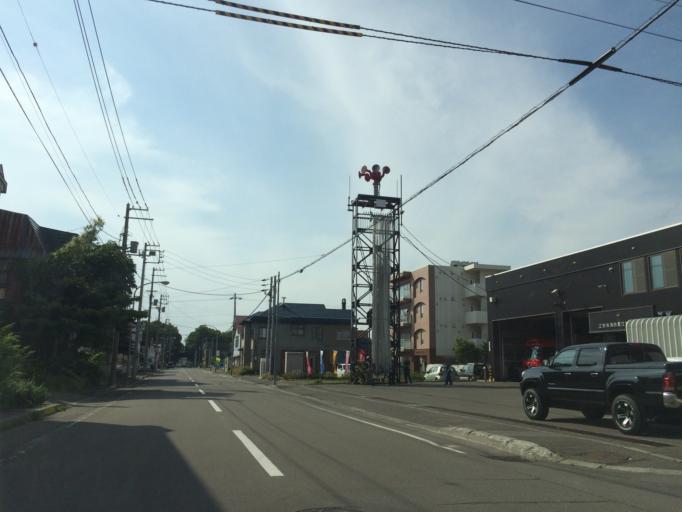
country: JP
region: Hokkaido
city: Ebetsu
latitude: 43.1137
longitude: 141.5592
